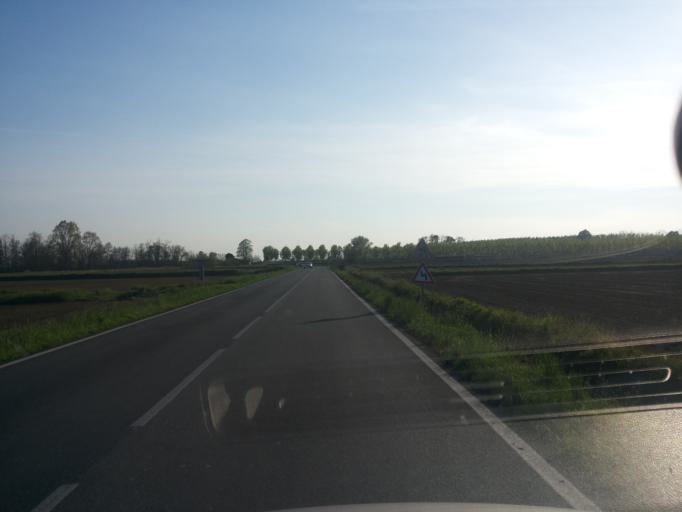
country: IT
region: Lombardy
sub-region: Provincia di Pavia
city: Zeme
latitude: 45.2060
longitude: 8.6402
